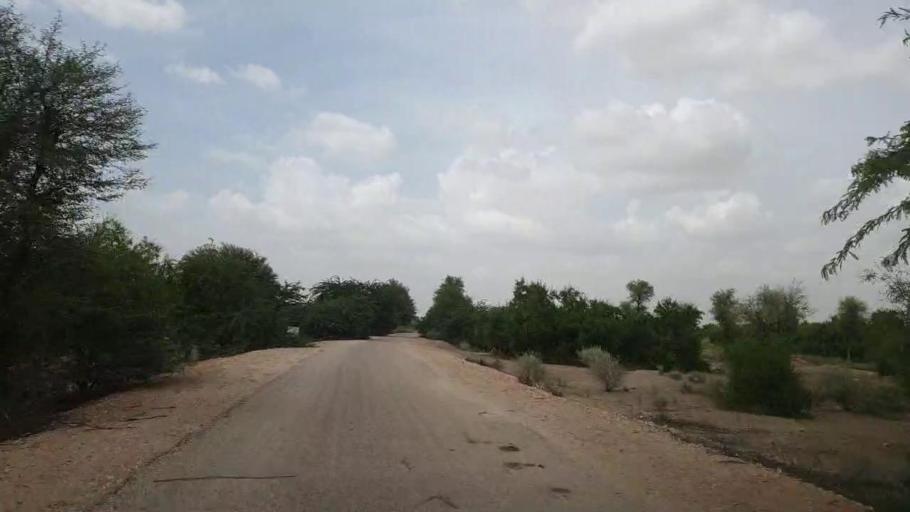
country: PK
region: Sindh
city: Kot Diji
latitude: 27.2205
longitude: 69.0841
